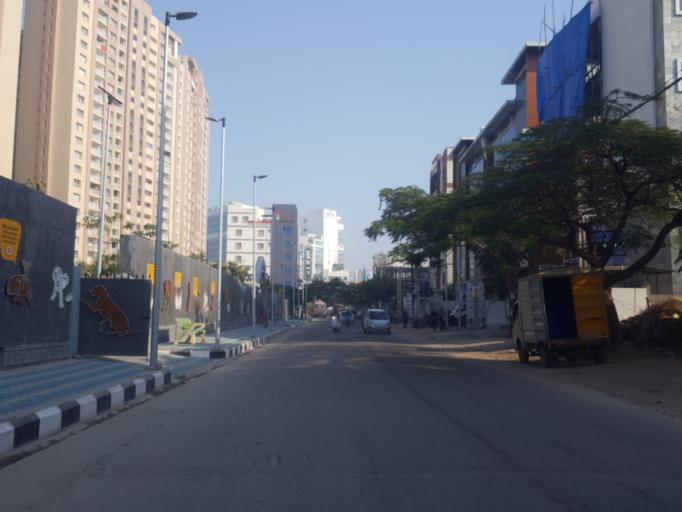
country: IN
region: Telangana
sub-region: Rangareddi
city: Kukatpalli
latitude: 17.4485
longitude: 78.3620
